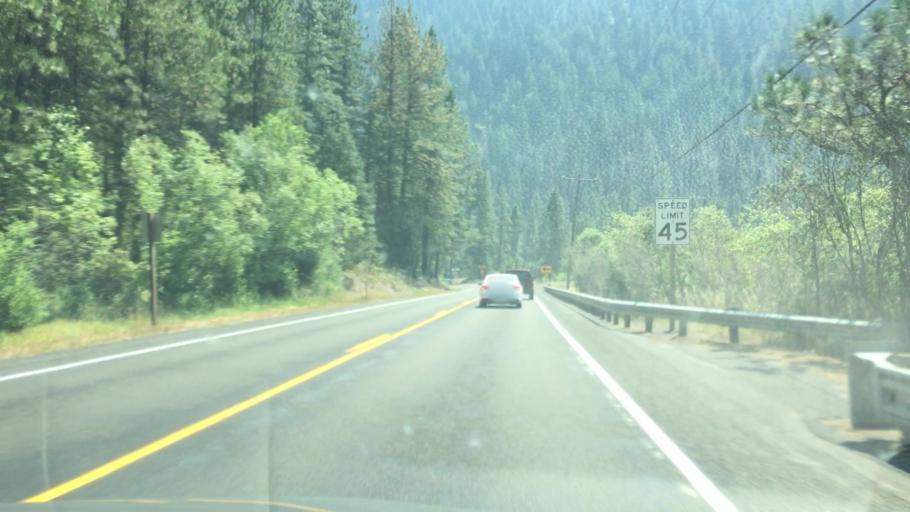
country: US
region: Idaho
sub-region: Valley County
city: McCall
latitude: 45.1511
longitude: -116.2967
